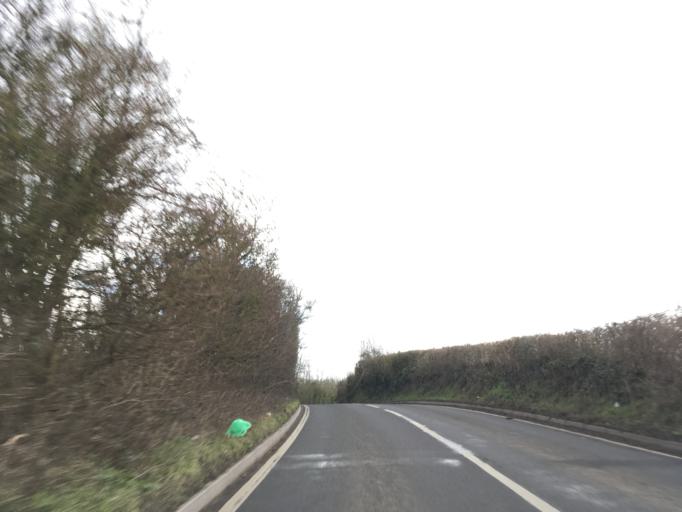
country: GB
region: England
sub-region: South Gloucestershire
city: Tytherington
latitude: 51.5636
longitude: -2.4929
